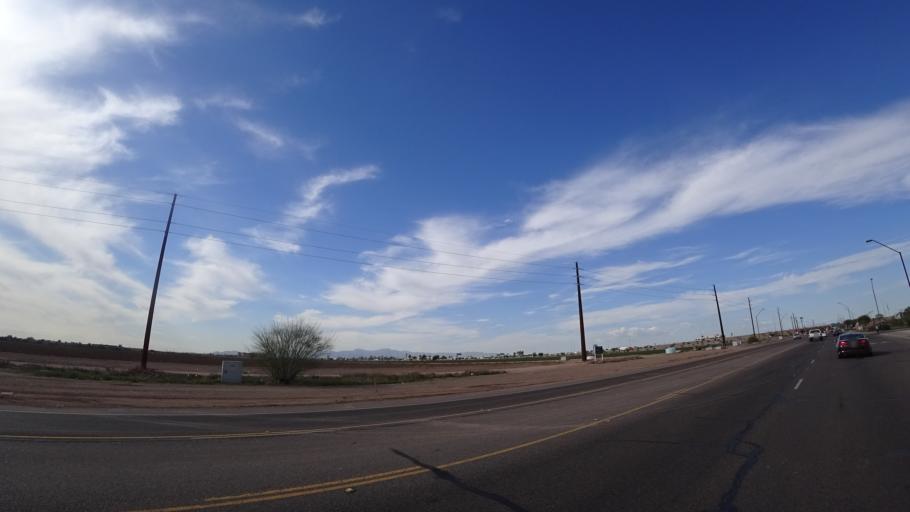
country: US
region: Arizona
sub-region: Maricopa County
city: Tolleson
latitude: 33.4560
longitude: -112.2898
